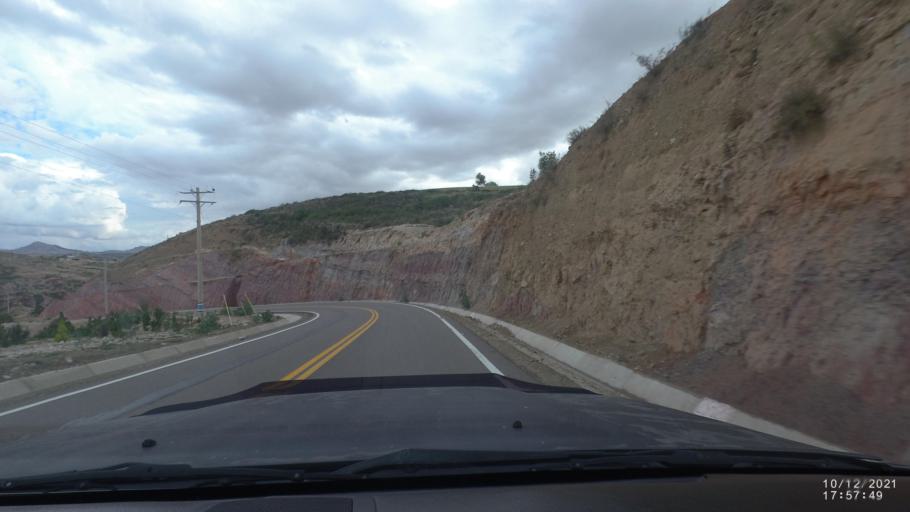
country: BO
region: Cochabamba
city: Cliza
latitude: -17.7217
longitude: -65.9323
